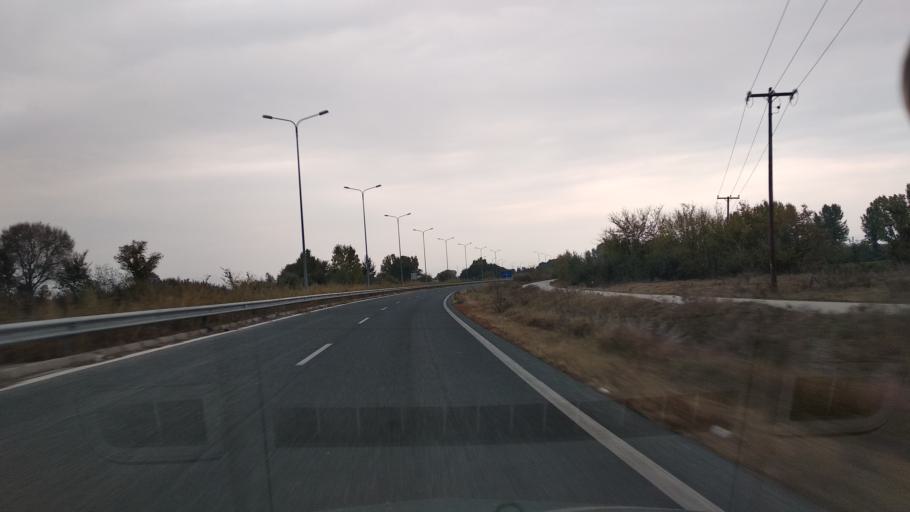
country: GR
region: Thessaly
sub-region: Trikala
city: Pyrgetos
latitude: 39.5374
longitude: 21.7365
